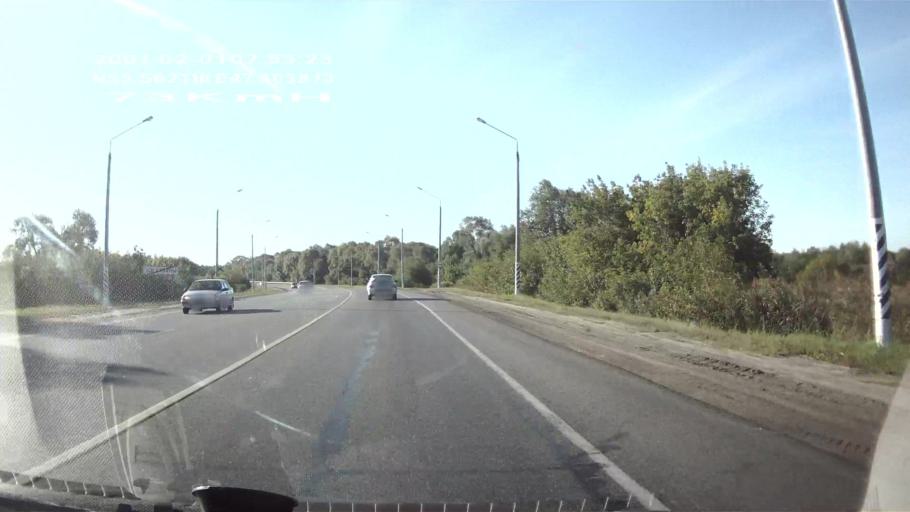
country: RU
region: Chuvashia
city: Shikhazany
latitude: 55.5619
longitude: 47.4040
